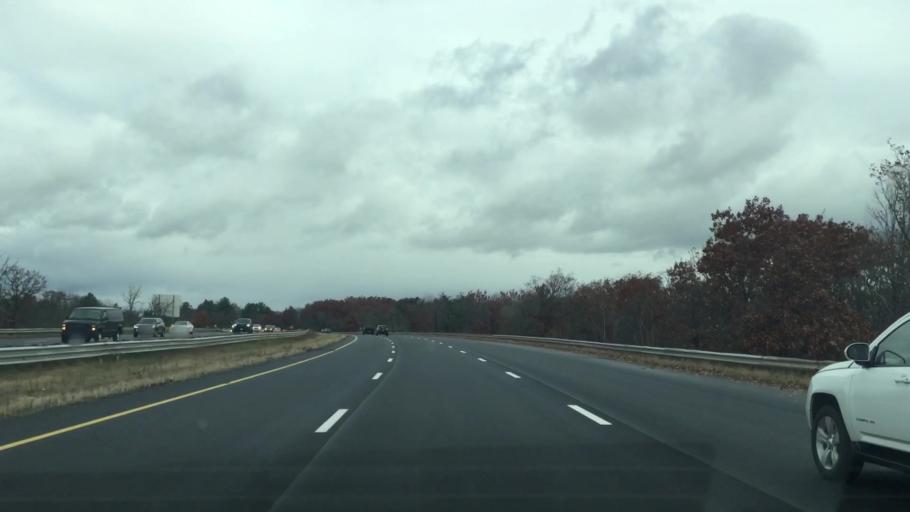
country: US
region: Massachusetts
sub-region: Essex County
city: Methuen
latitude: 42.7329
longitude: -71.2034
